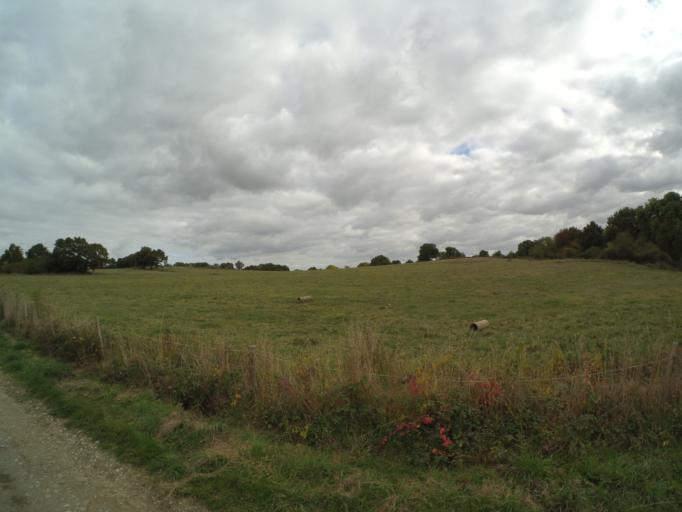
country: FR
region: Pays de la Loire
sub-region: Departement de la Loire-Atlantique
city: Remouille
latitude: 47.0530
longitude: -1.3566
